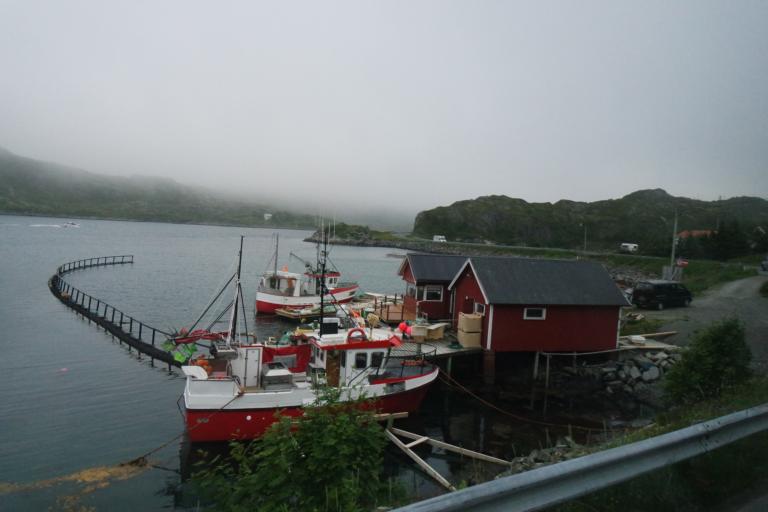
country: NO
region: Nordland
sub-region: Flakstad
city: Ramberg
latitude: 68.0230
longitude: 13.1852
